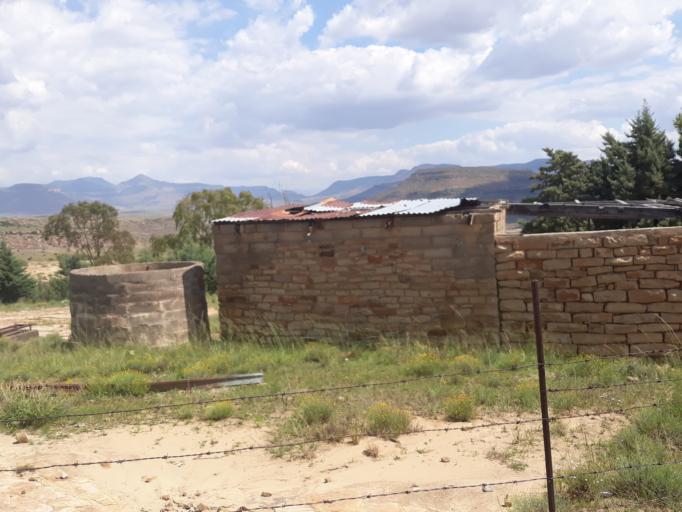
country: LS
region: Quthing
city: Quthing
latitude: -30.3426
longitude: 27.5281
